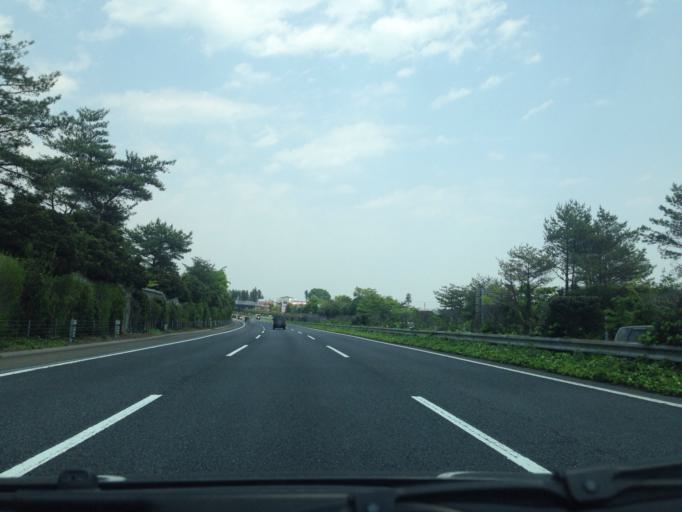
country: JP
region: Tochigi
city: Kanuma
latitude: 36.5309
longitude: 139.7923
